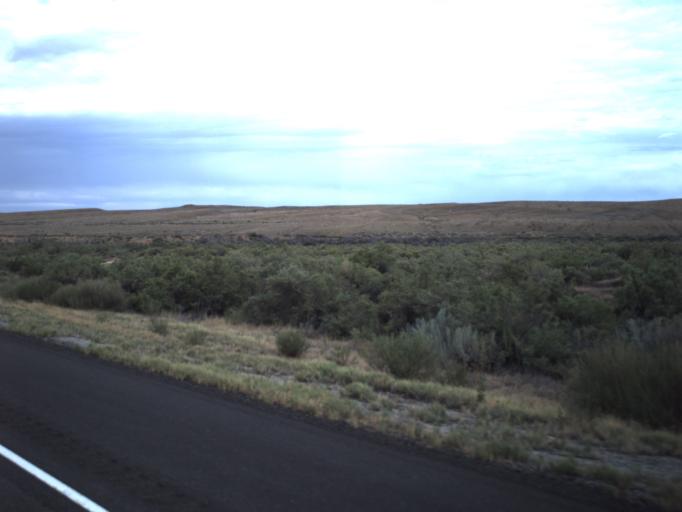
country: US
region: Colorado
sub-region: Mesa County
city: Loma
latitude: 39.0795
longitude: -109.2276
